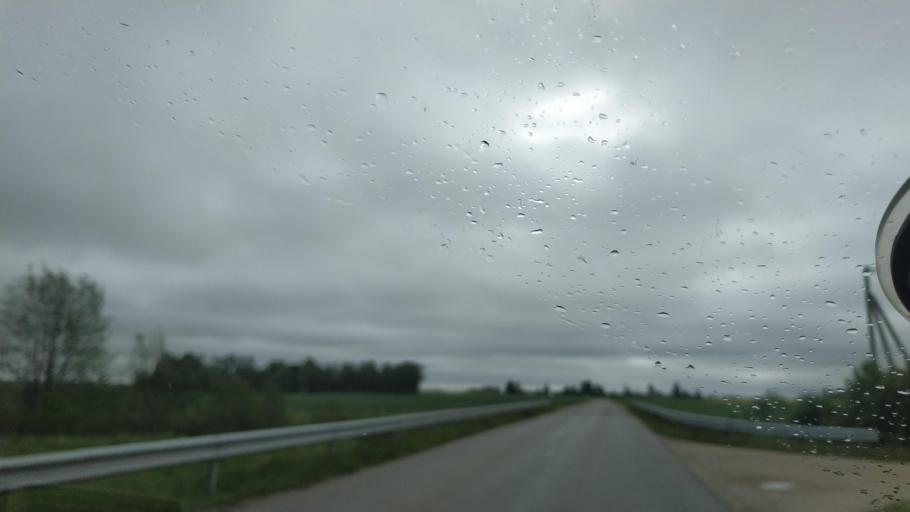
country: LT
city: Vabalninkas
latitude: 55.9933
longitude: 24.6864
